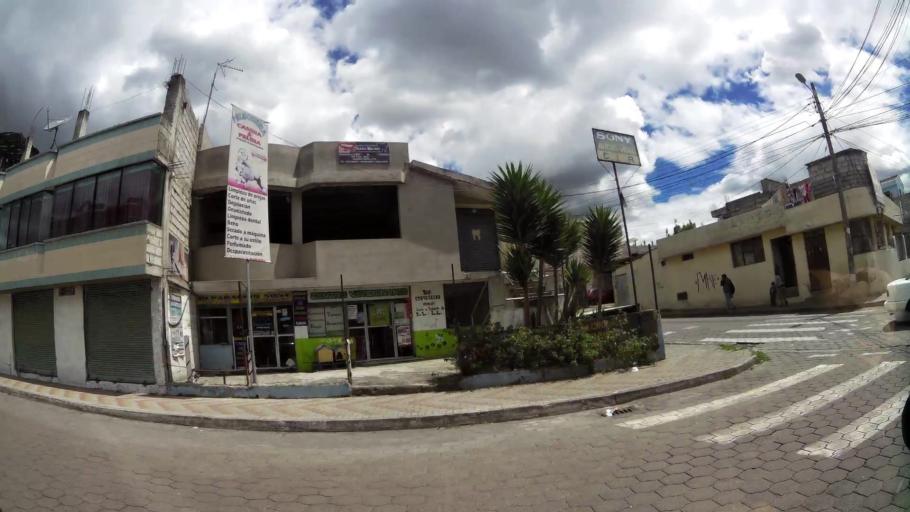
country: EC
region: Pichincha
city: Sangolqui
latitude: -0.3354
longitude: -78.5450
